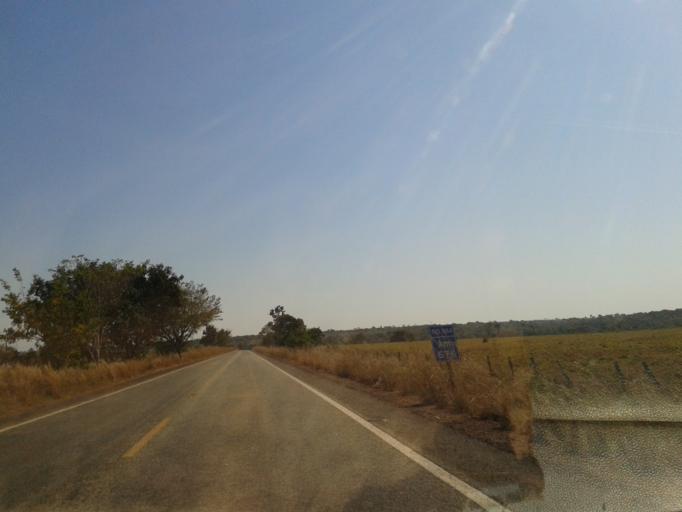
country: BR
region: Goias
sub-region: Mozarlandia
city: Mozarlandia
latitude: -14.5007
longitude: -50.4846
